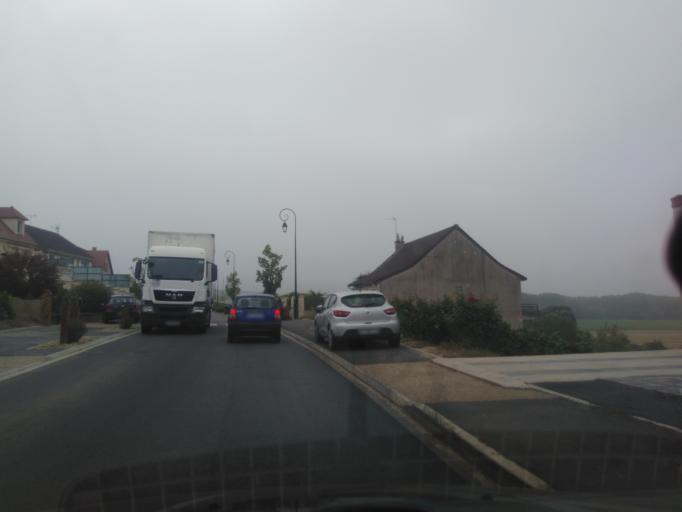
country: FR
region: Champagne-Ardenne
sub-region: Departement de la Marne
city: Mardeuil
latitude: 49.0727
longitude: 3.9332
